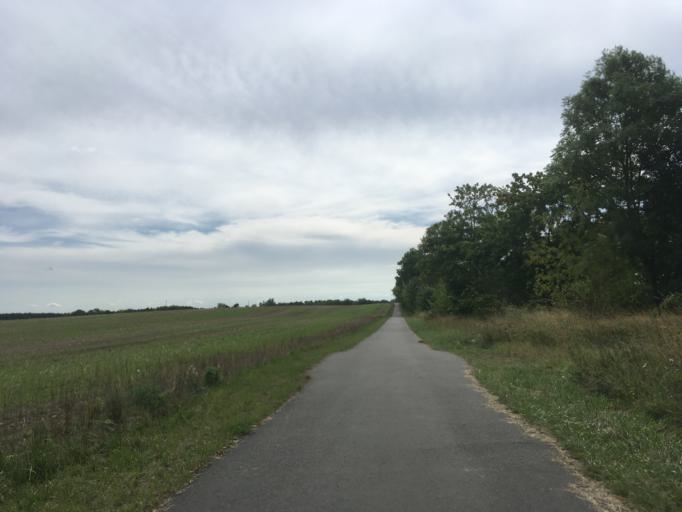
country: DE
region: Brandenburg
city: Mittenwalde
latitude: 53.2323
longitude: 13.6545
